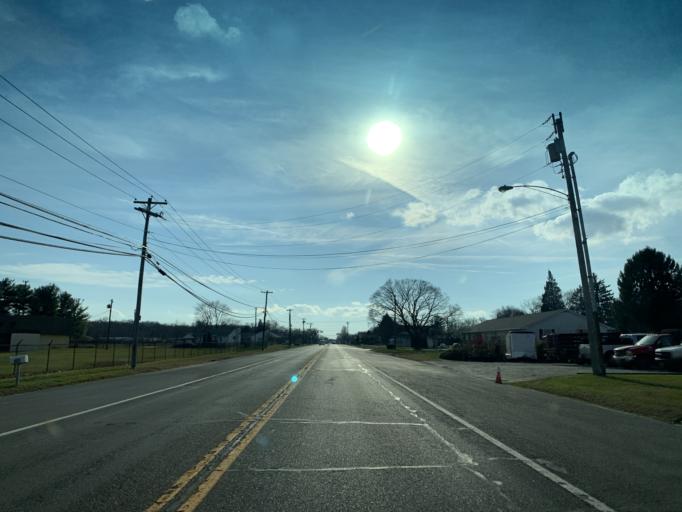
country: US
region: New Jersey
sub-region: Salem County
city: Penns Grove
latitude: 39.7431
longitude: -75.4551
